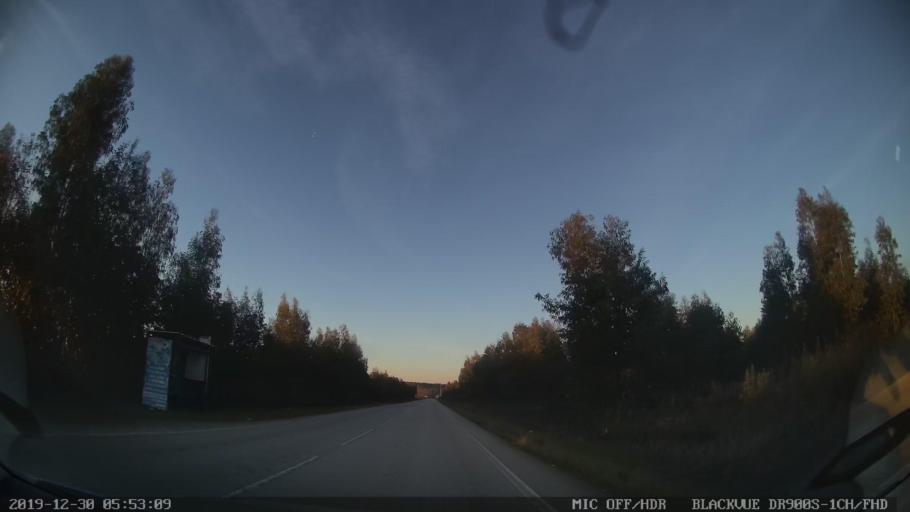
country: PT
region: Castelo Branco
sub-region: Idanha-A-Nova
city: Idanha-a-Nova
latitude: 40.0127
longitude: -7.2501
